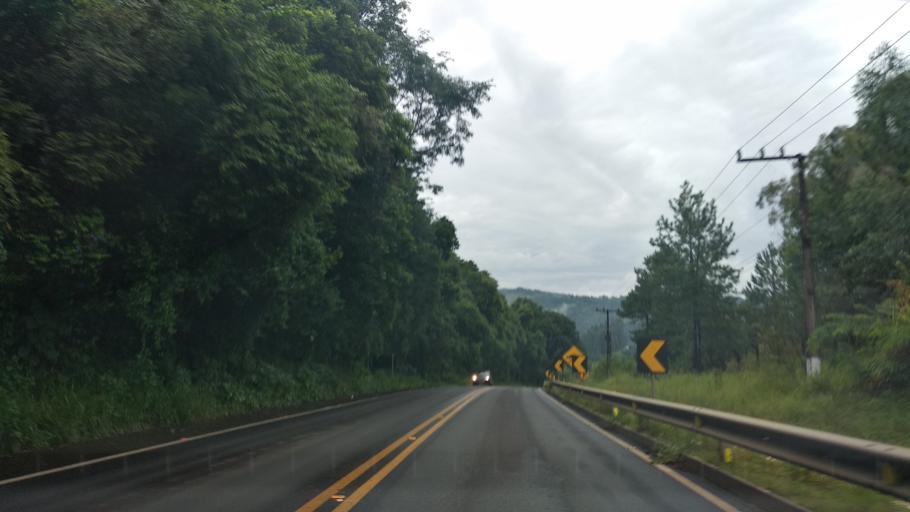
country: BR
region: Santa Catarina
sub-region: Videira
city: Videira
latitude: -27.0518
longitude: -51.2300
